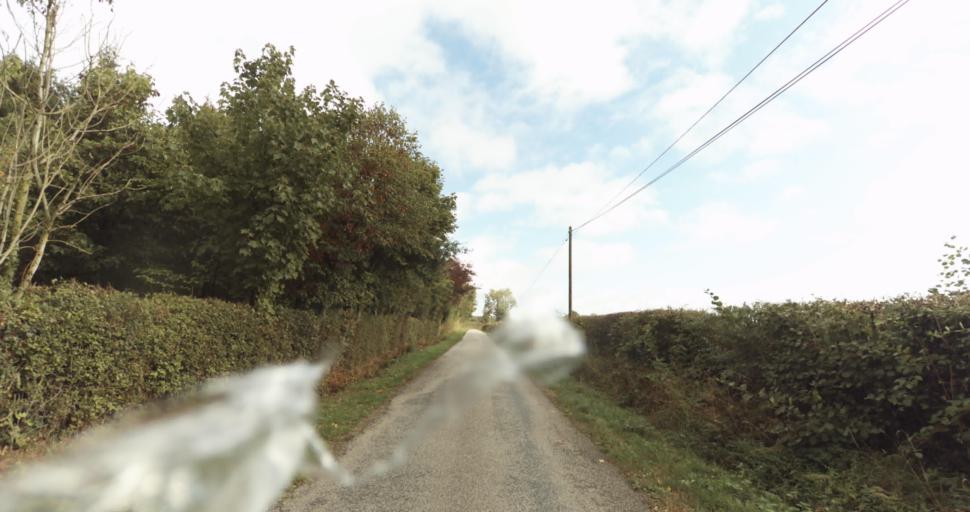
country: FR
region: Lower Normandy
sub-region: Departement de l'Orne
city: Gace
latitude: 48.8560
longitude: 0.3240
